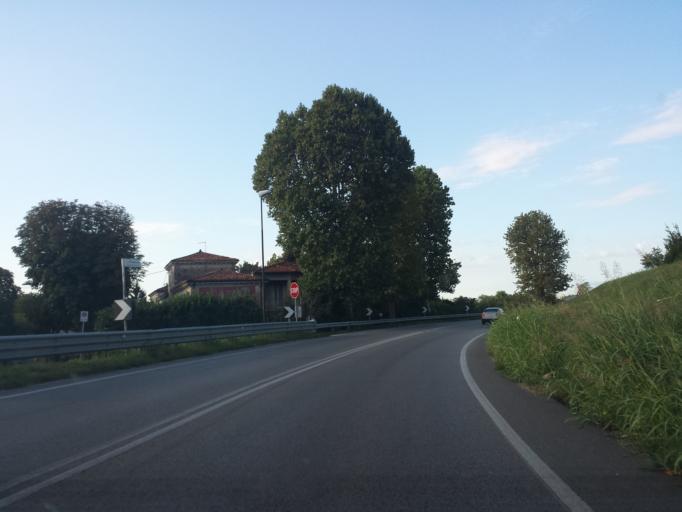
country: IT
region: Veneto
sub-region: Provincia di Vicenza
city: Montebello Vicentino
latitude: 45.4552
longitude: 11.3900
